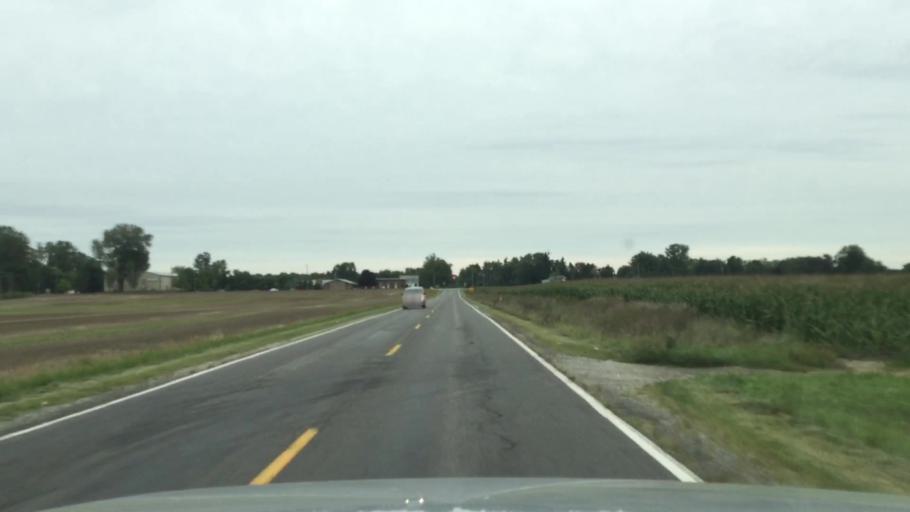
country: US
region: Michigan
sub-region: Washtenaw County
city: Milan
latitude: 42.1202
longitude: -83.6961
